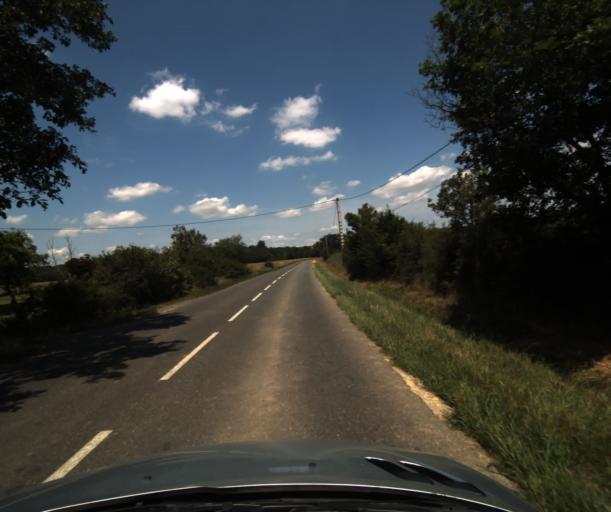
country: FR
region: Midi-Pyrenees
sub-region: Departement de la Haute-Garonne
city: Labastidette
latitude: 43.4868
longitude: 1.2139
